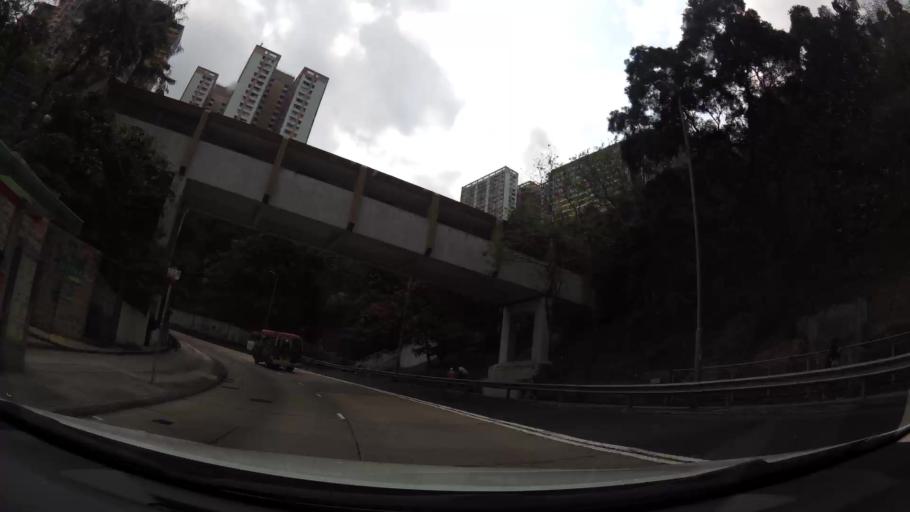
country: HK
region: Kowloon City
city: Kowloon
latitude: 22.3225
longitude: 114.2184
